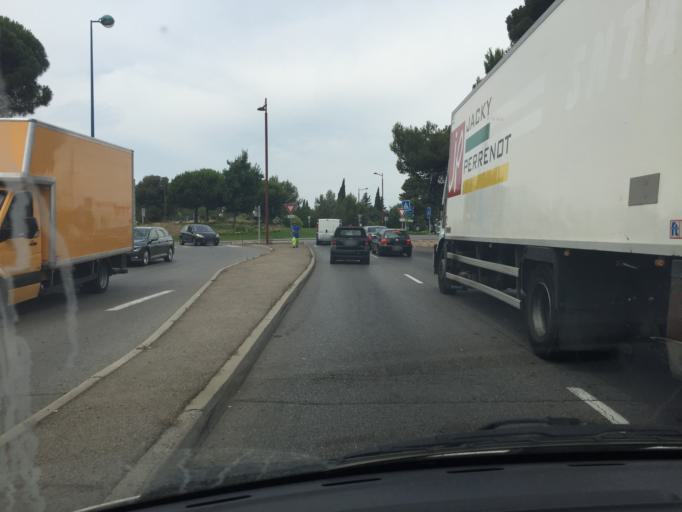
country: FR
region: Provence-Alpes-Cote d'Azur
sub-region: Departement des Alpes-Maritimes
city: Biot
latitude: 43.5960
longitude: 7.0910
